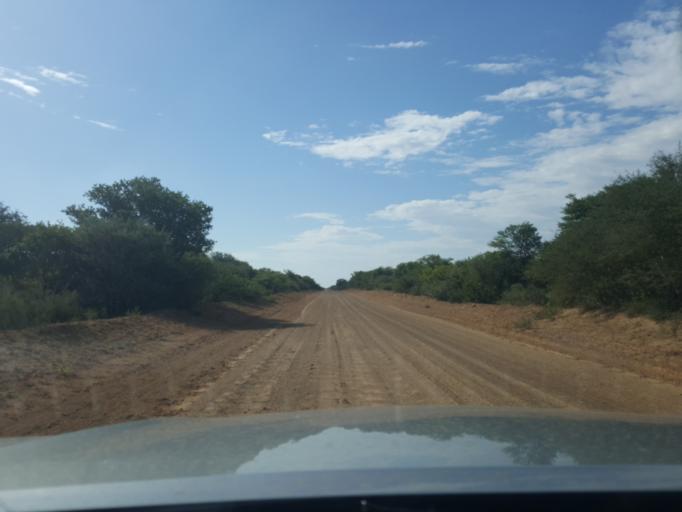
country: BW
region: Kweneng
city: Khudumelapye
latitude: -23.5142
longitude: 24.7150
